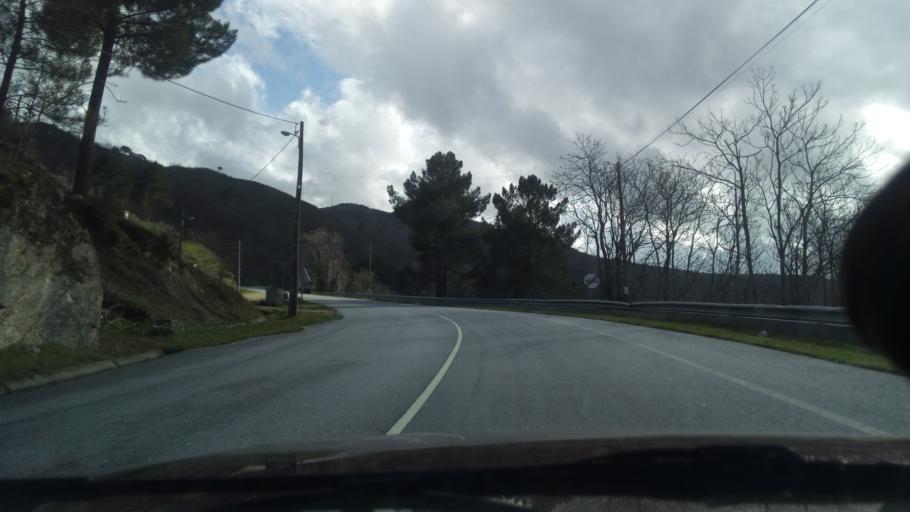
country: PT
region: Guarda
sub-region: Guarda
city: Guarda
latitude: 40.5689
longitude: -7.2983
